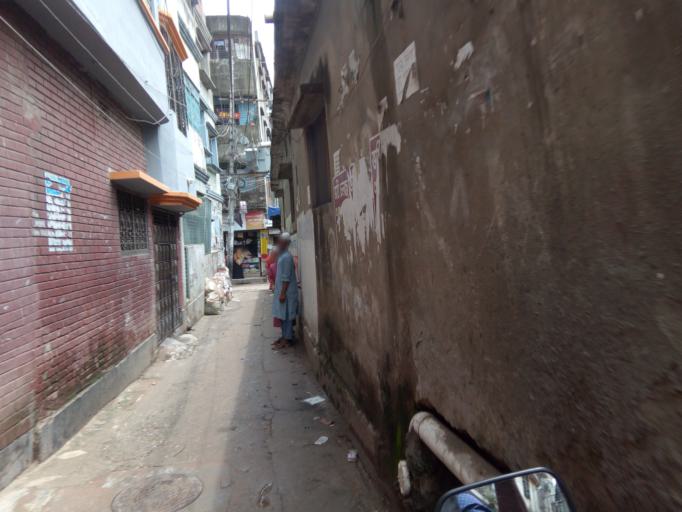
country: BD
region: Dhaka
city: Azimpur
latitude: 23.7259
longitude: 90.3743
